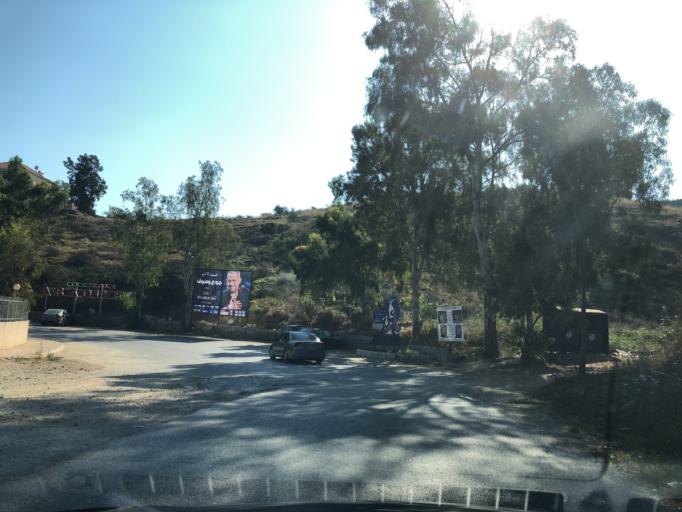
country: LB
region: Mont-Liban
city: Aaley
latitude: 33.8182
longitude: 35.6151
